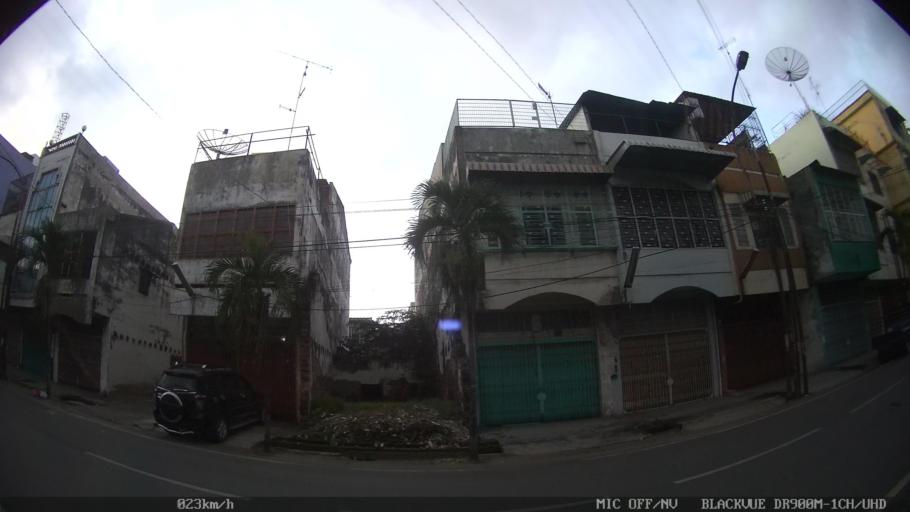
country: ID
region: North Sumatra
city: Medan
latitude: 3.5811
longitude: 98.6934
